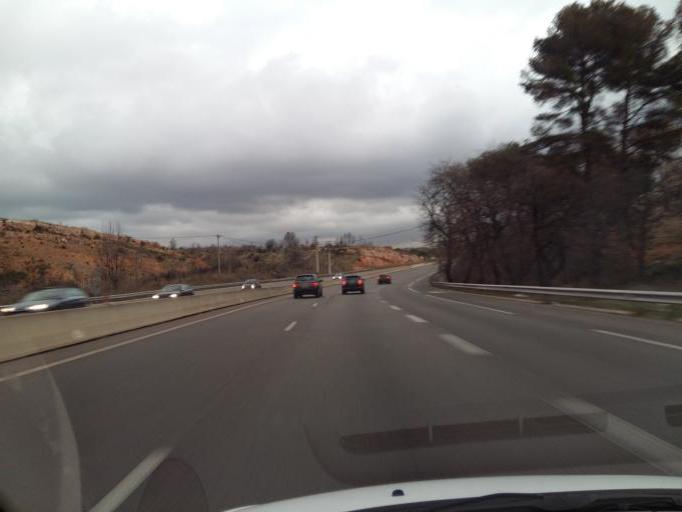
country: FR
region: Provence-Alpes-Cote d'Azur
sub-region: Departement des Bouches-du-Rhone
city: Vitrolles
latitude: 43.4358
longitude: 5.2813
